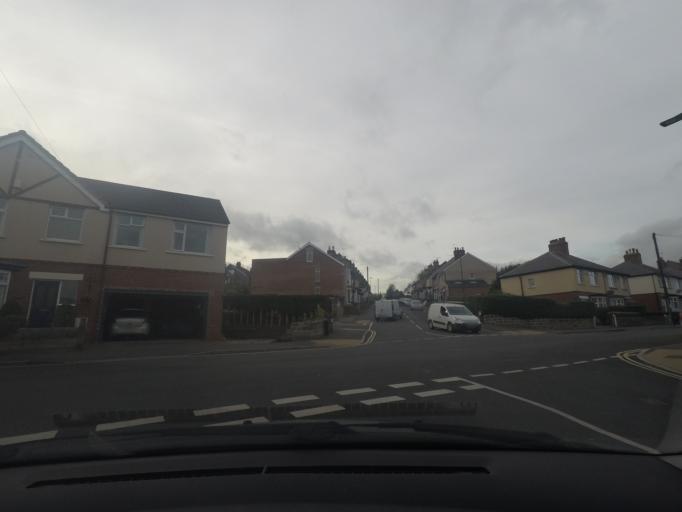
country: GB
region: England
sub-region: Sheffield
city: Oughtibridge
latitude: 53.4089
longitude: -1.5062
